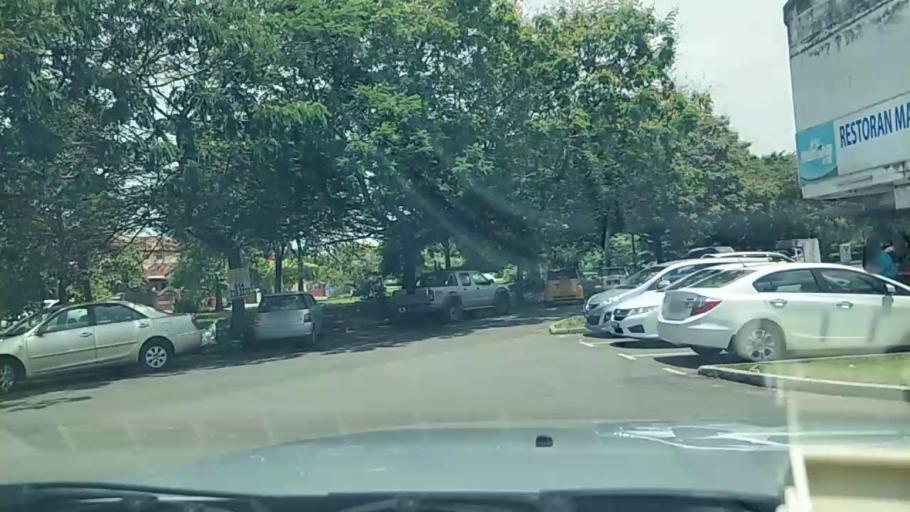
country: MY
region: Putrajaya
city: Putrajaya
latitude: 2.9467
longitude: 101.6179
